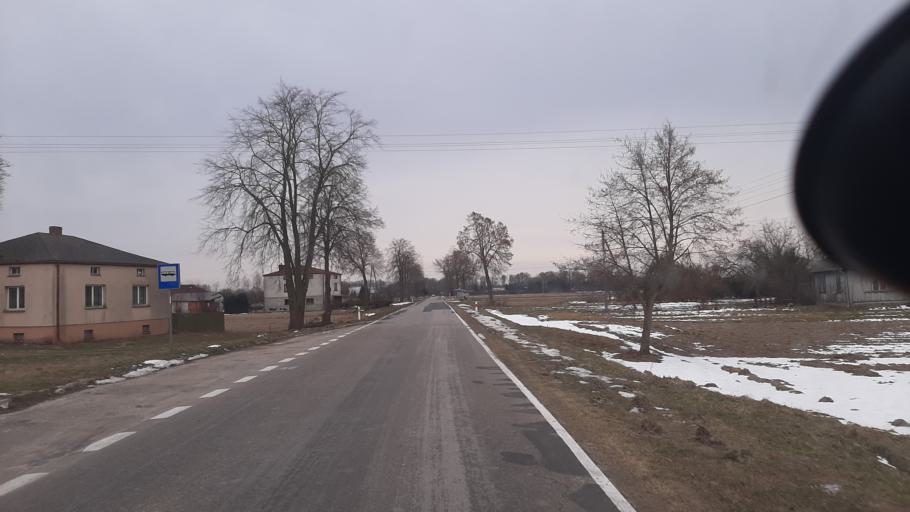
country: PL
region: Lublin Voivodeship
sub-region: Powiat lubartowski
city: Kamionka
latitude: 51.4546
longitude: 22.4211
